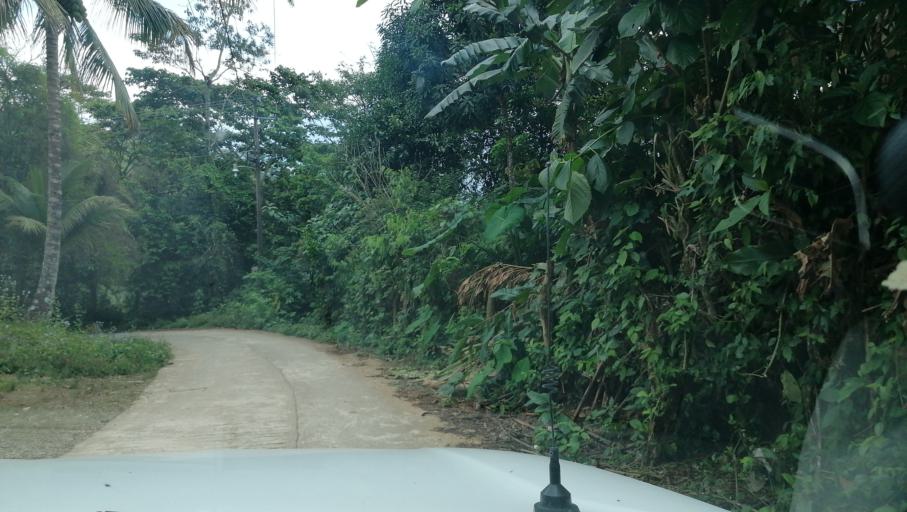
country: MX
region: Chiapas
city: Ixtacomitan
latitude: 17.3567
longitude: -93.1171
